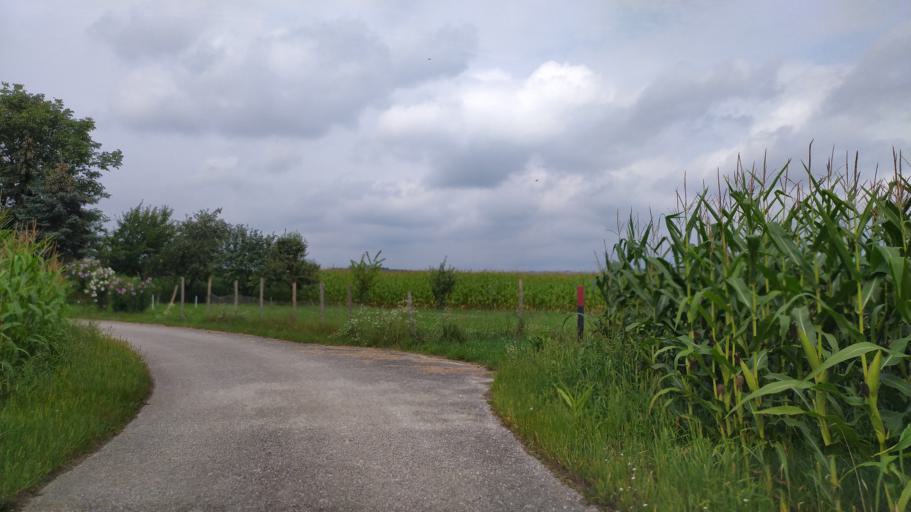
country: AT
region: Lower Austria
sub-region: Politischer Bezirk Amstetten
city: Zeillern
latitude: 48.1912
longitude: 14.7643
